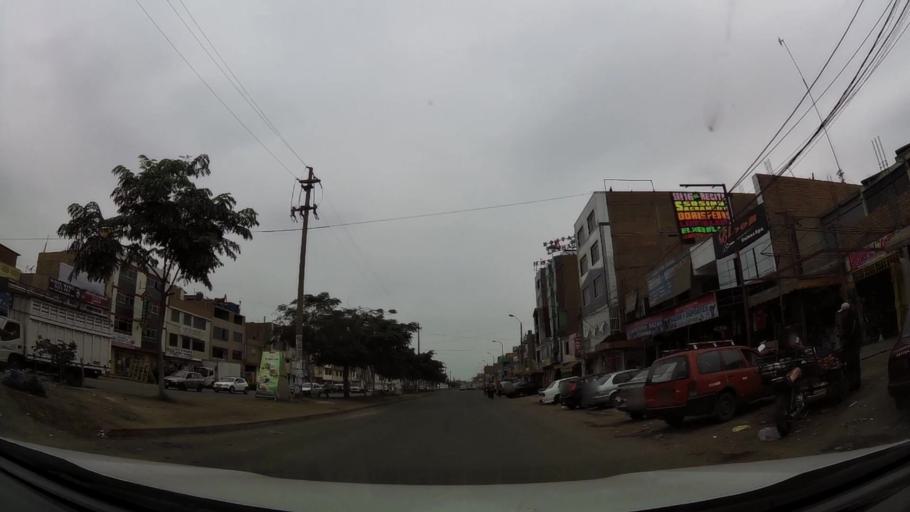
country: PE
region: Lima
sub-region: Lima
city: Independencia
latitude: -11.9773
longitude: -77.0836
